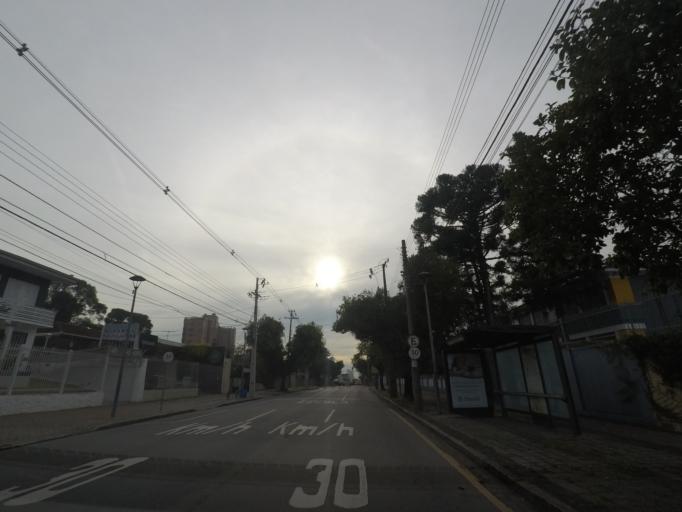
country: BR
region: Parana
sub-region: Curitiba
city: Curitiba
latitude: -25.4394
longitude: -49.2925
